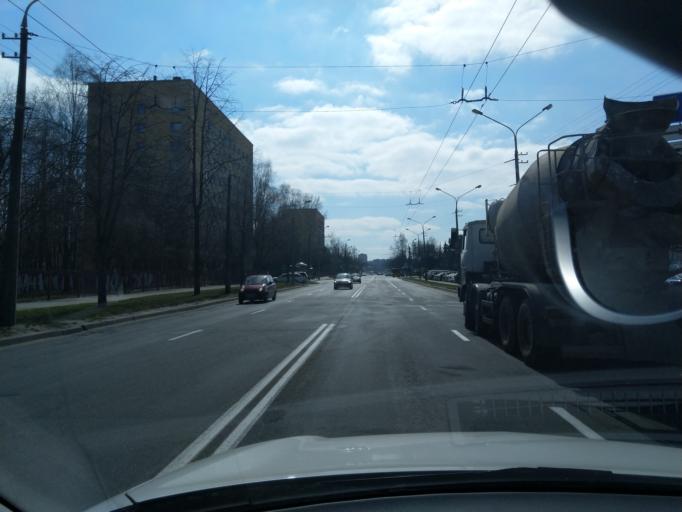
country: BY
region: Minsk
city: Syenitsa
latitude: 53.8615
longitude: 27.4973
